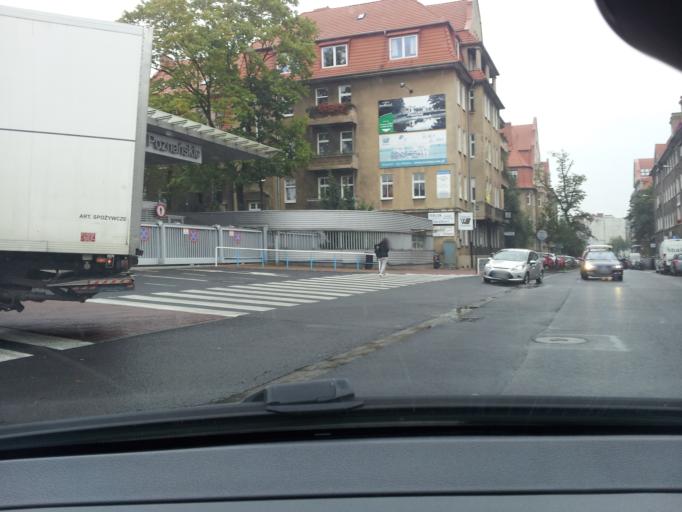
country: PL
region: Greater Poland Voivodeship
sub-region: Poznan
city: Poznan
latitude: 52.4023
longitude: 16.9035
